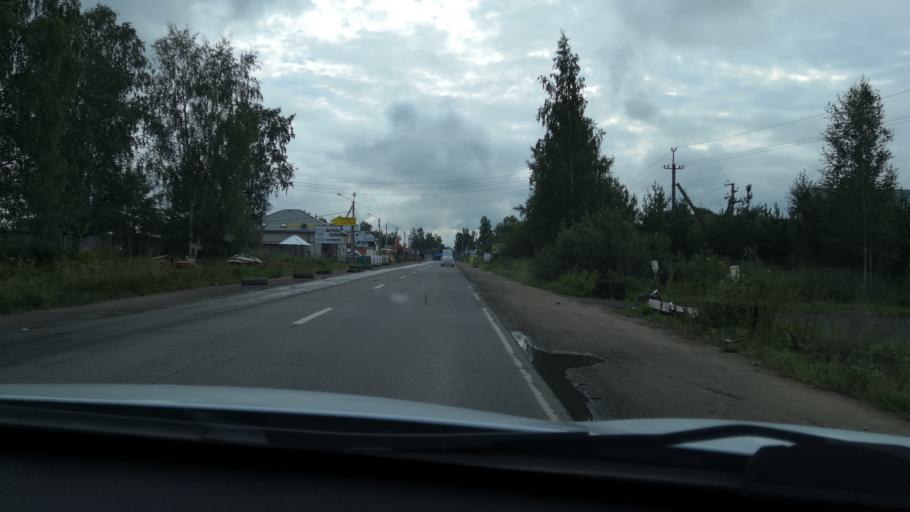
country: RU
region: St.-Petersburg
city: Kolpino
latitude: 59.7044
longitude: 30.5732
